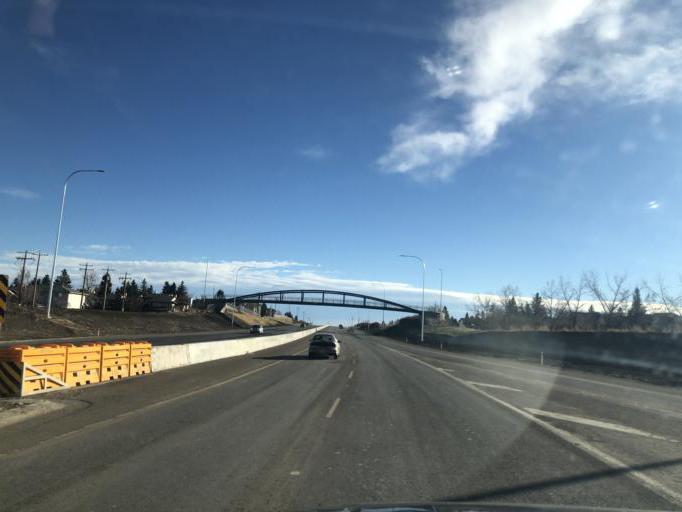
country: CA
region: Alberta
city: Calgary
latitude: 50.9505
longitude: -114.1344
